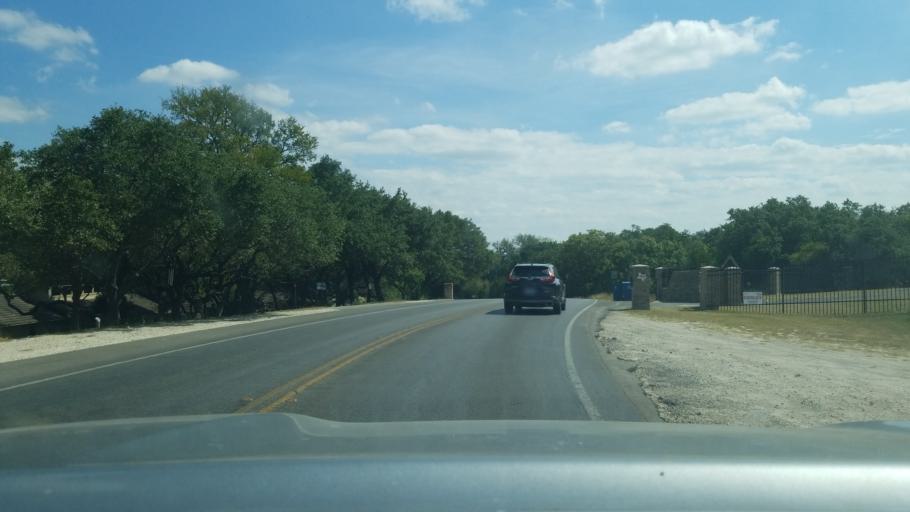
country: US
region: Texas
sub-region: Bexar County
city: Fair Oaks Ranch
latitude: 29.7314
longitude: -98.6337
